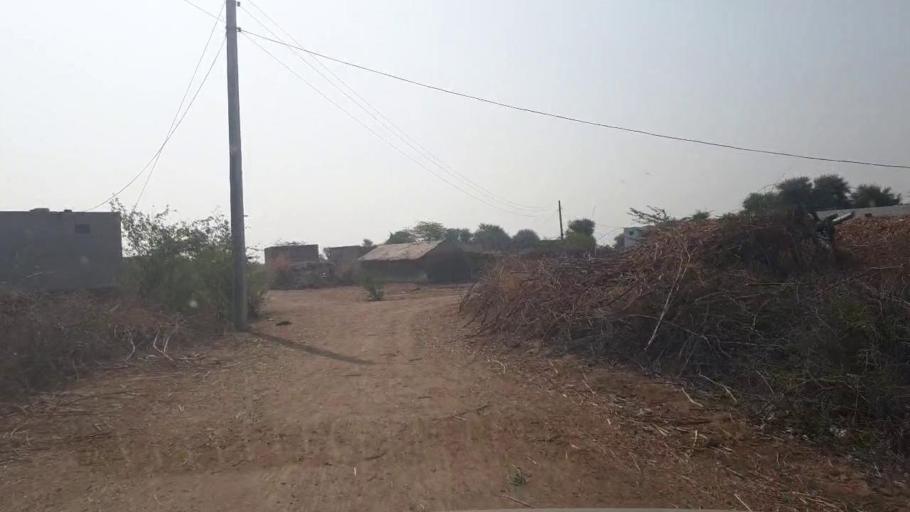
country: PK
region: Sindh
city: Umarkot
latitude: 25.4010
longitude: 69.6910
